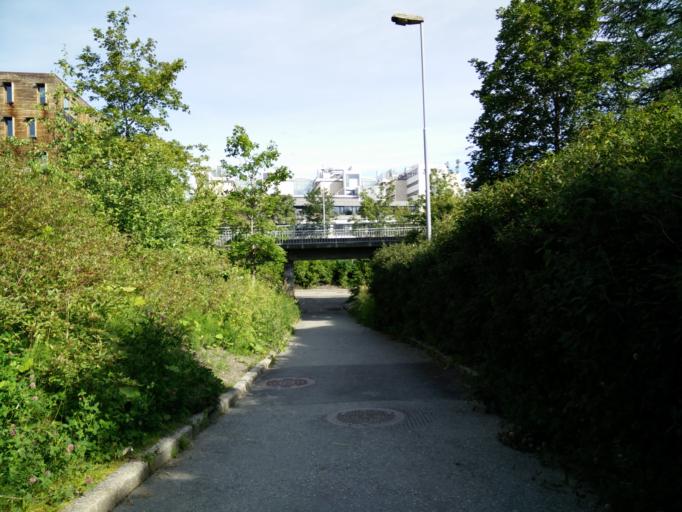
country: NO
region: Sor-Trondelag
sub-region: Trondheim
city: Trondheim
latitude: 63.4134
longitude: 10.4080
